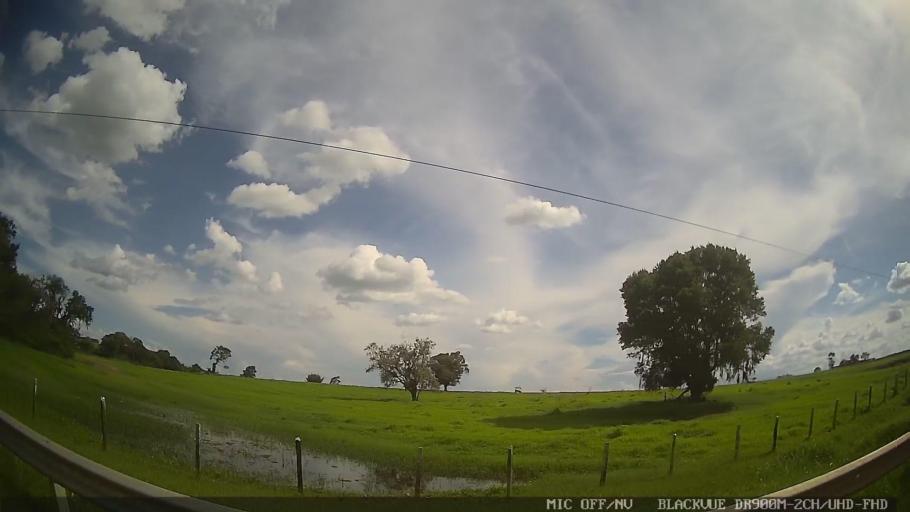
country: BR
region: Sao Paulo
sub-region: Conchas
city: Conchas
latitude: -23.0451
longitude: -47.9440
